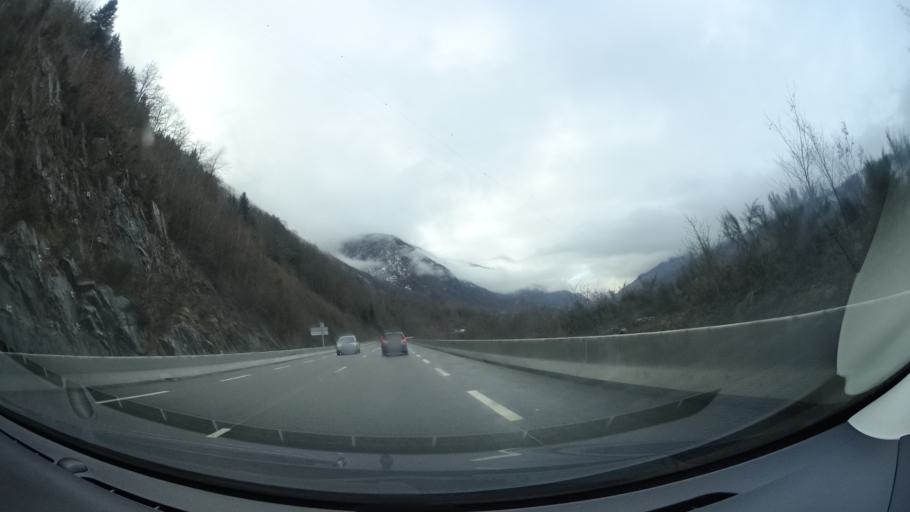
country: FR
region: Midi-Pyrenees
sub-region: Departement de l'Ariege
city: Ax-les-Thermes
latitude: 42.7254
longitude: 1.8143
